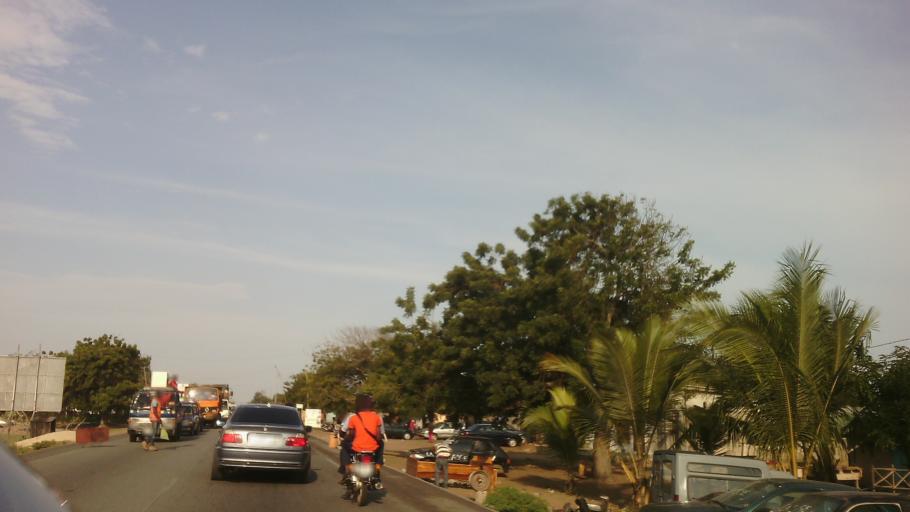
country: TG
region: Maritime
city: Lome
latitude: 6.1769
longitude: 1.3700
